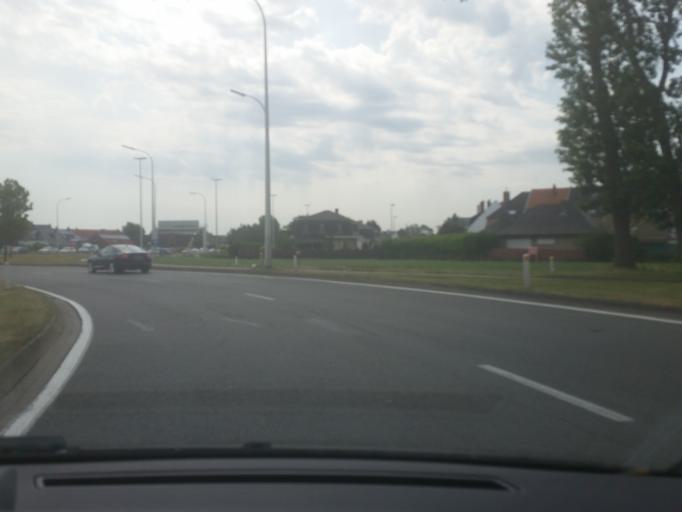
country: BE
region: Flanders
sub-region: Provincie West-Vlaanderen
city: Ostend
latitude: 51.2149
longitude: 2.9282
